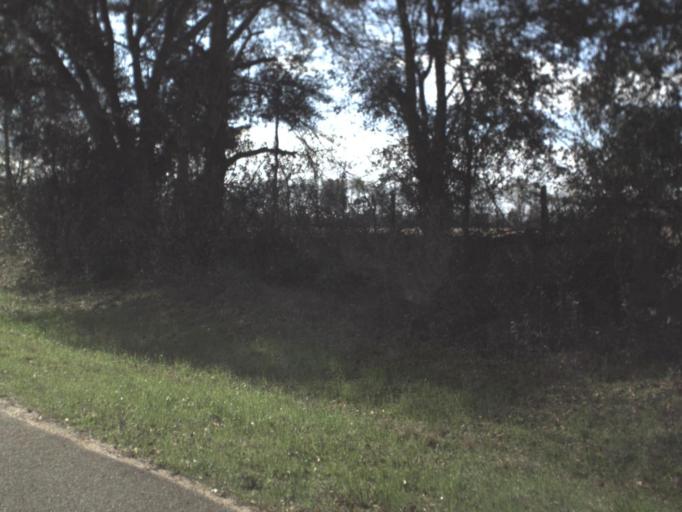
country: US
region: Florida
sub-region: Jackson County
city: Malone
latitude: 30.9932
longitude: -85.1950
